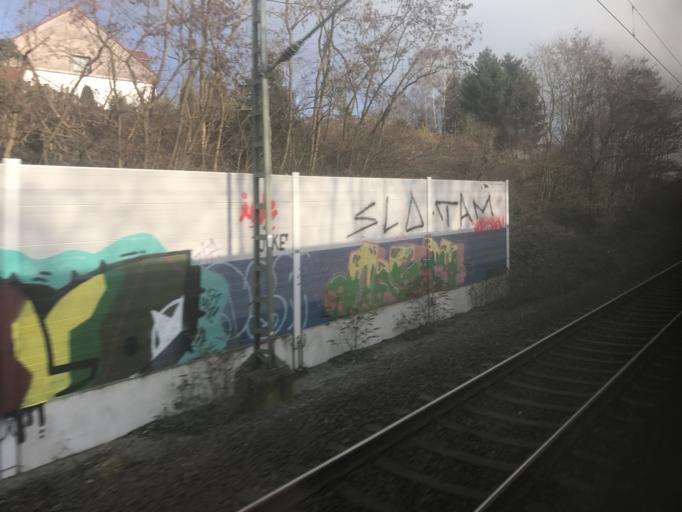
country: DE
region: North Rhine-Westphalia
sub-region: Regierungsbezirk Arnsberg
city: Bochum
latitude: 51.4863
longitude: 7.2652
